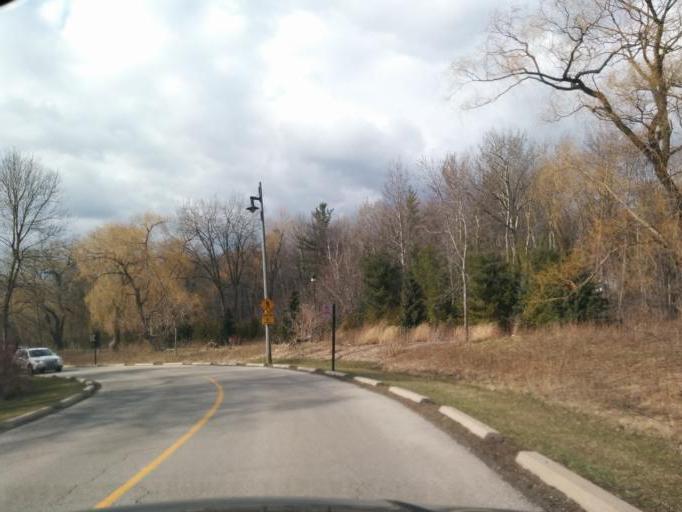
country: CA
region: Ontario
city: Mississauga
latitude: 43.5285
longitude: -79.6046
